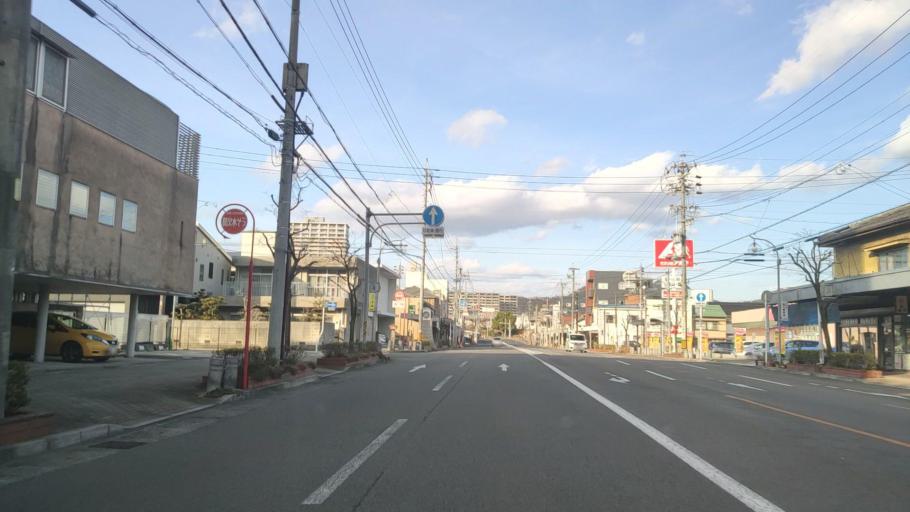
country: JP
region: Gifu
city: Gifu-shi
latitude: 35.4049
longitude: 136.7589
